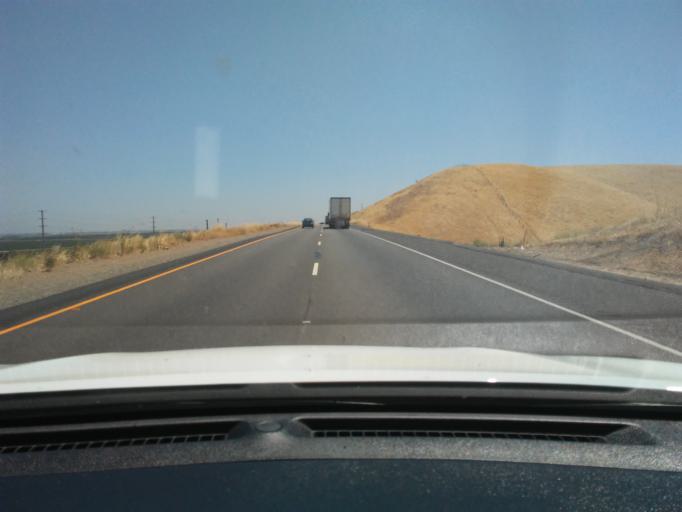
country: US
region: California
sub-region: Stanislaus County
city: Patterson
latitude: 37.4567
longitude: -121.1753
